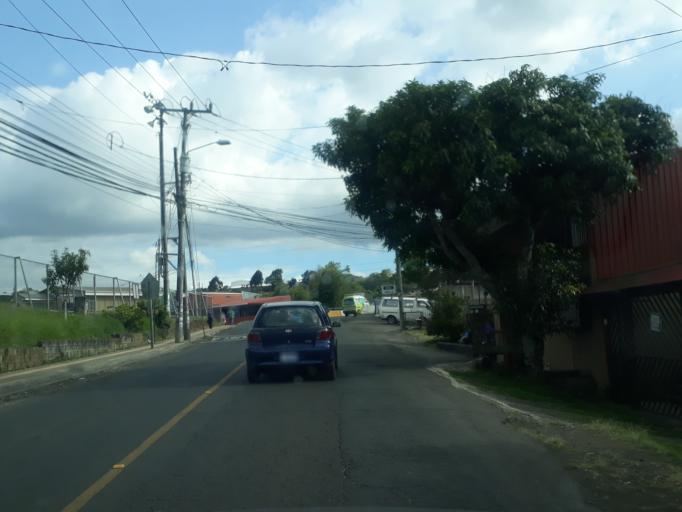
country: CR
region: Heredia
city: Angeles
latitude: 9.9927
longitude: -84.0257
